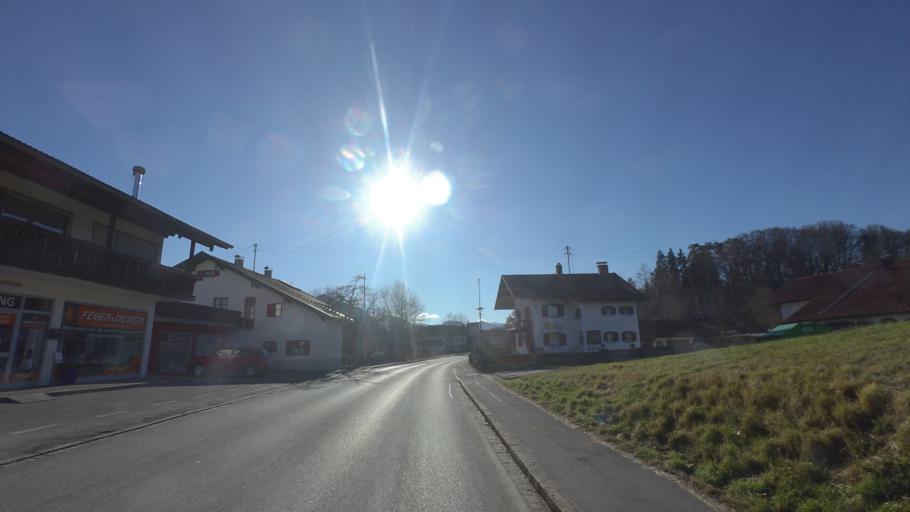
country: DE
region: Bavaria
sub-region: Upper Bavaria
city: Ubersee
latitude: 47.8157
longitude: 12.4825
